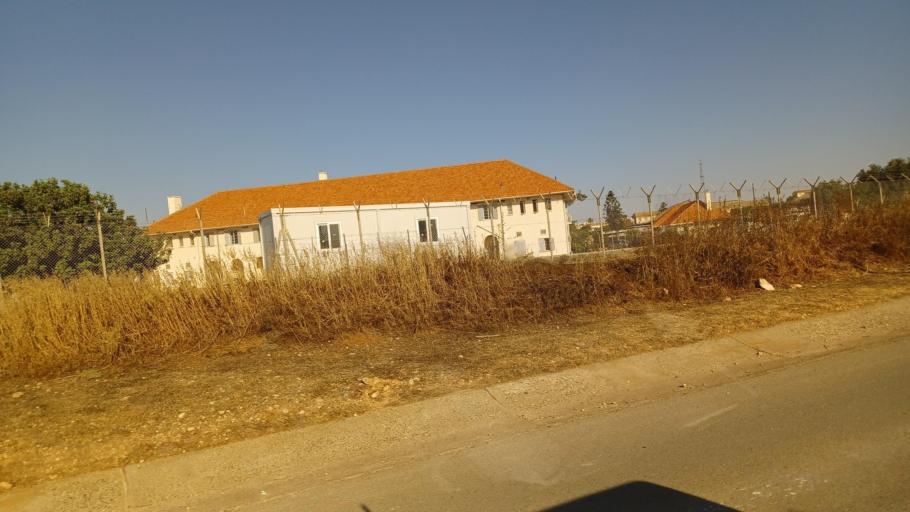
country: CY
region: Larnaka
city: Xylotymbou
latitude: 34.9960
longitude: 33.7425
